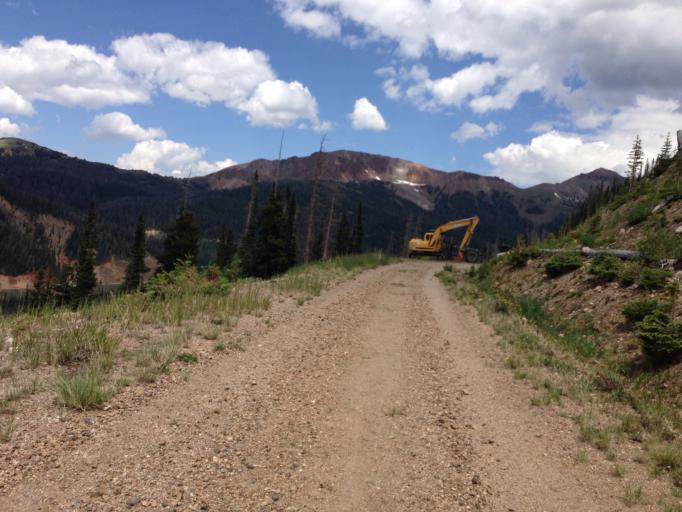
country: US
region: Colorado
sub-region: Larimer County
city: Estes Park
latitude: 40.4964
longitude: -105.8965
